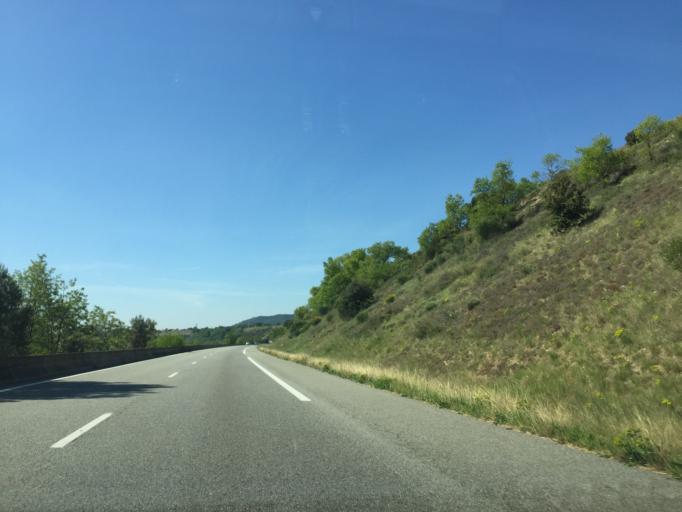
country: FR
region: Provence-Alpes-Cote d'Azur
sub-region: Departement des Alpes-de-Haute-Provence
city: Oraison
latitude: 43.9497
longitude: 5.8967
